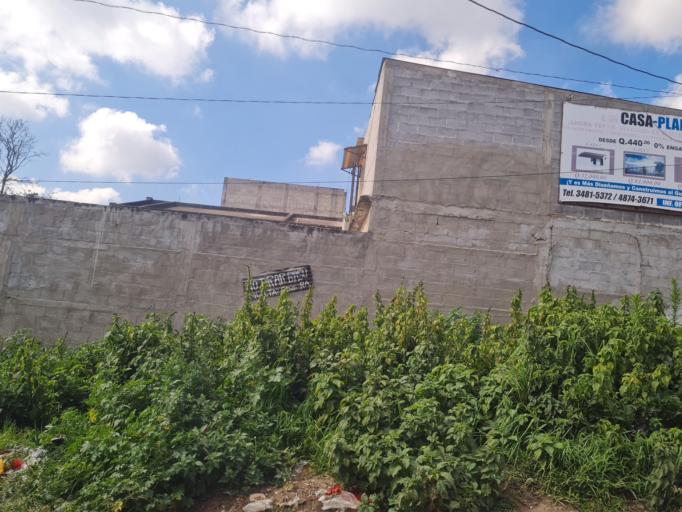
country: GT
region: Quetzaltenango
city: Quetzaltenango
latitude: 14.8439
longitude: -91.5332
